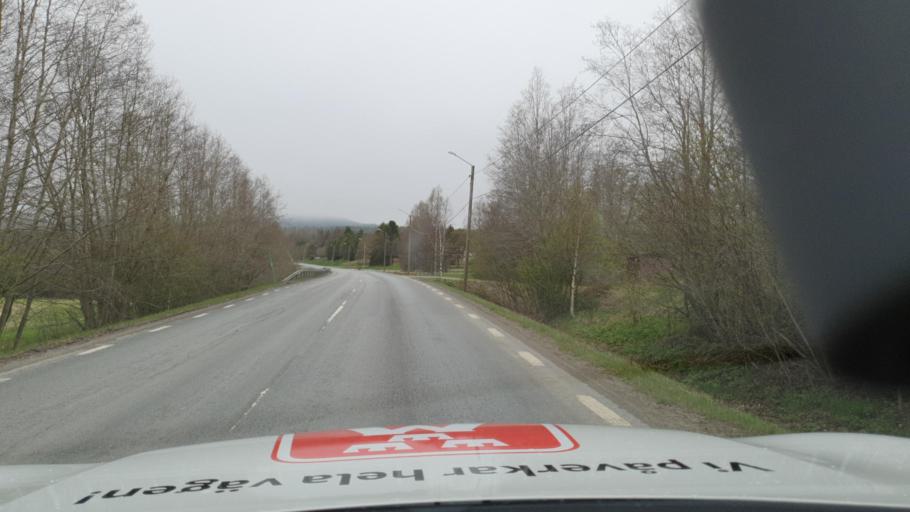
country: SE
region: Vaesterbotten
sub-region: Vannas Kommun
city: Vaennaes
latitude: 63.7750
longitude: 19.6701
